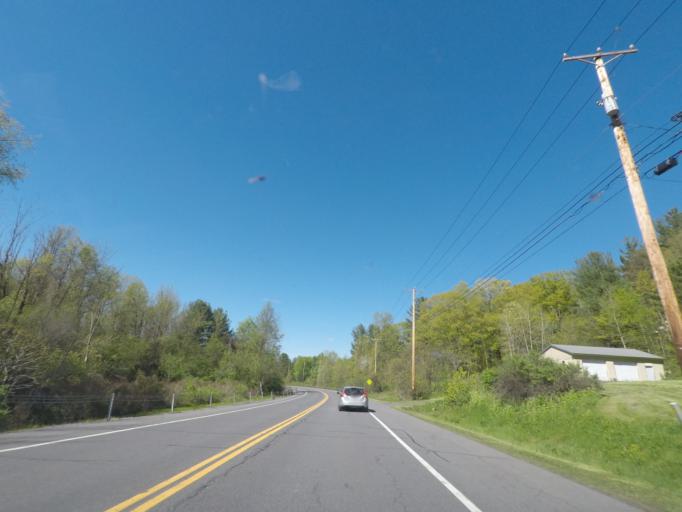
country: US
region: New York
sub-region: Albany County
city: Ravena
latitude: 42.4379
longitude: -73.8142
